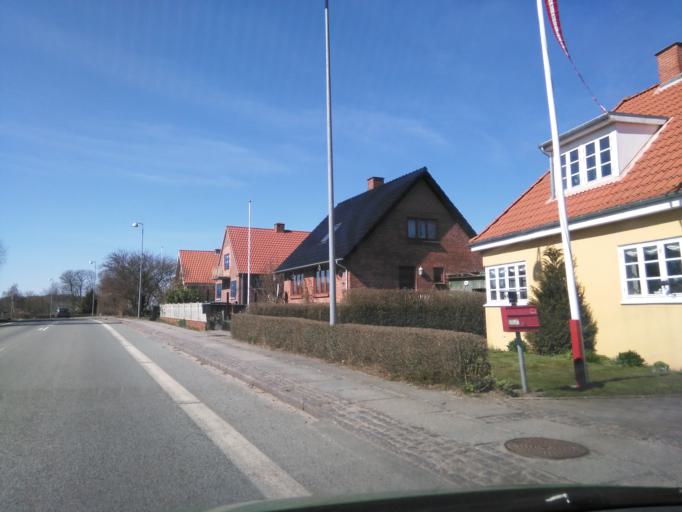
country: DK
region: Central Jutland
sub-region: Skanderborg Kommune
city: Ry
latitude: 56.0243
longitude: 9.7304
